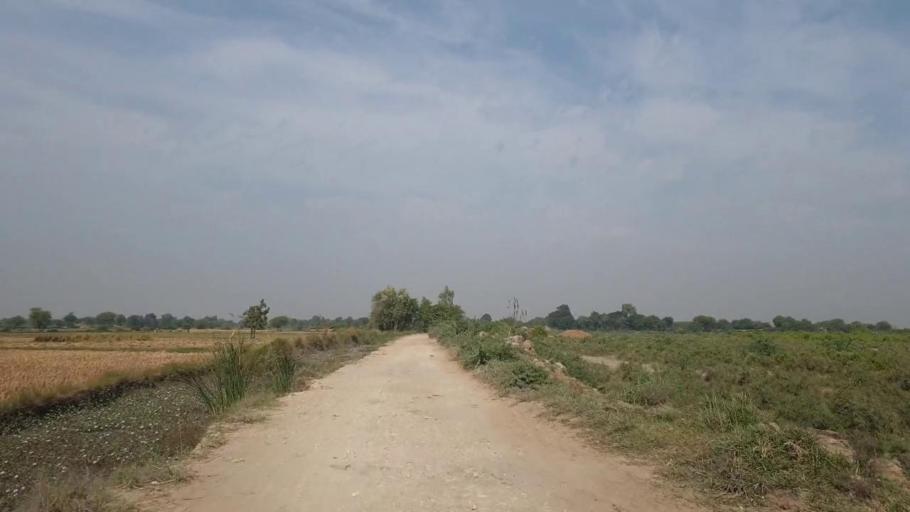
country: PK
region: Sindh
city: Tando Bago
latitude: 24.8894
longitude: 69.0021
